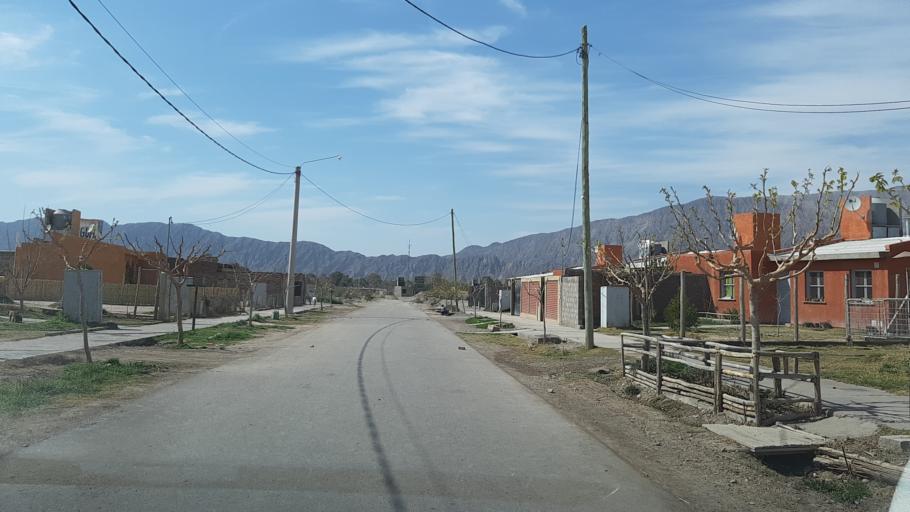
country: AR
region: San Juan
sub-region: Departamento de Zonda
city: Zonda
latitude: -31.5473
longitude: -68.7413
